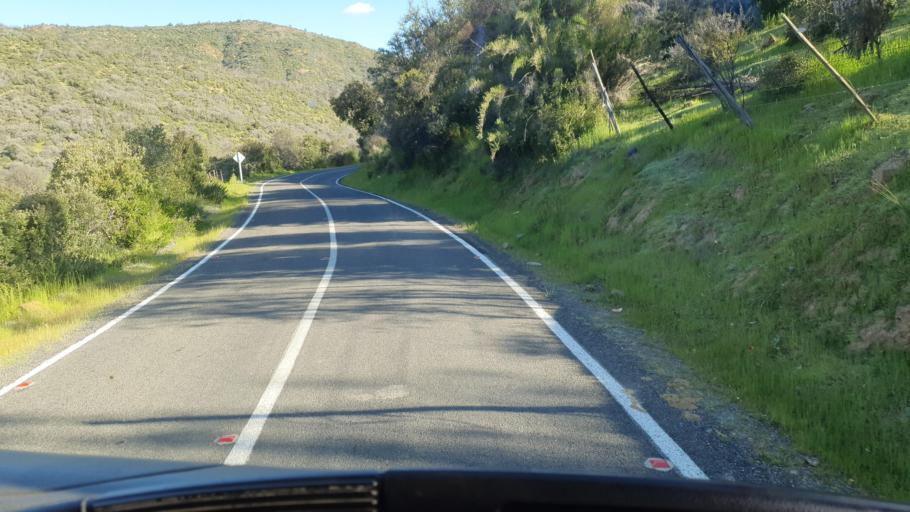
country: CL
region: Valparaiso
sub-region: Provincia de Marga Marga
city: Limache
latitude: -33.1813
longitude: -71.1732
